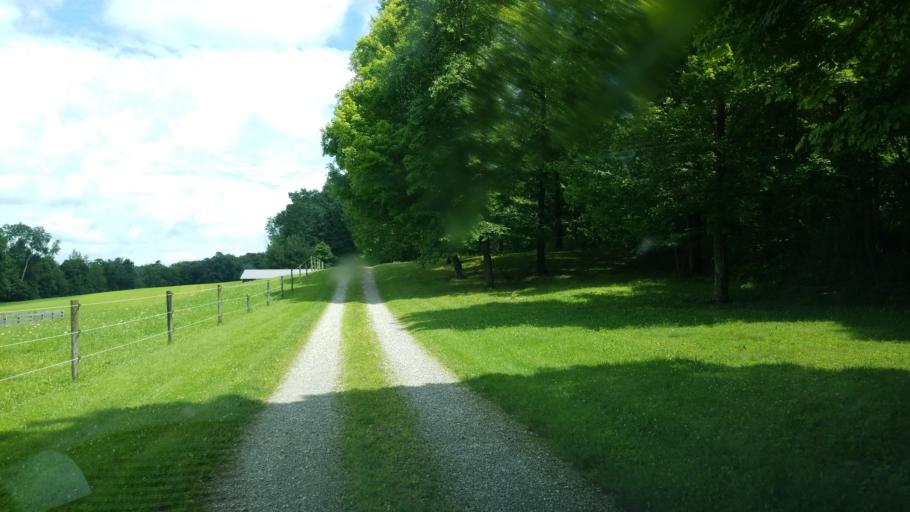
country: US
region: Ohio
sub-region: Sandusky County
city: Bellville
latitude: 40.6153
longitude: -82.5402
